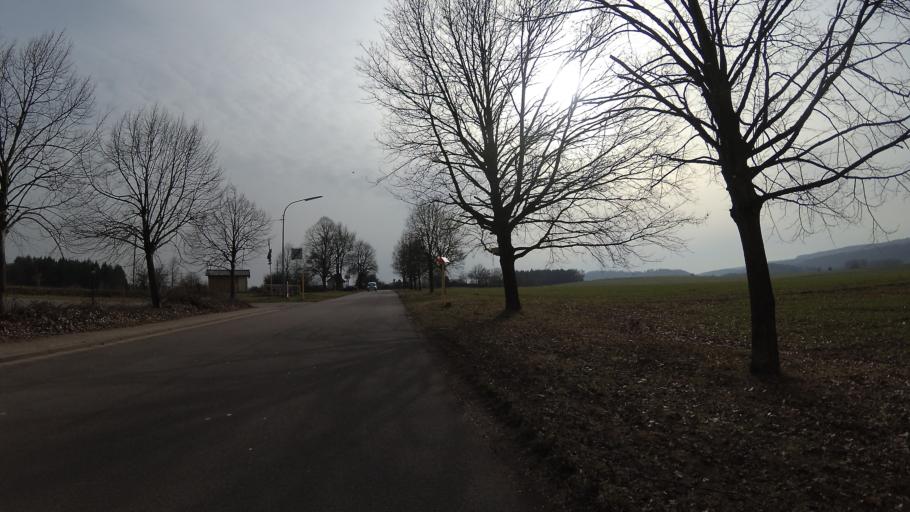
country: DE
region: Saarland
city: Nalbach
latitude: 49.4432
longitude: 6.7651
